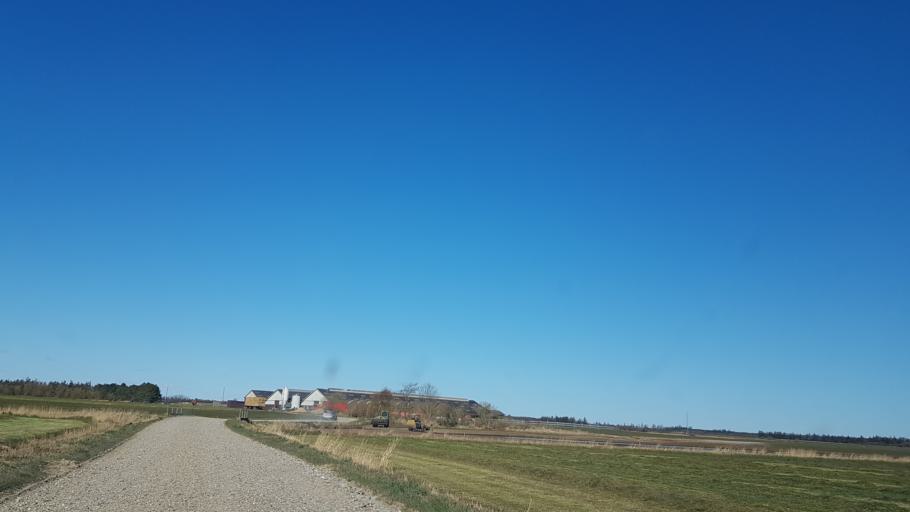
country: DK
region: South Denmark
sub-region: Tonder Kommune
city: Sherrebek
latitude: 55.2408
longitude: 8.7125
